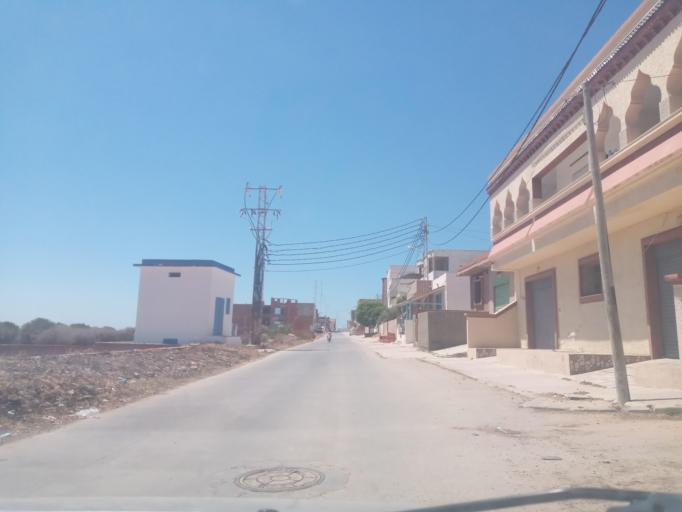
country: TN
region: Nabul
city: El Haouaria
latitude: 37.0491
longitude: 11.0050
